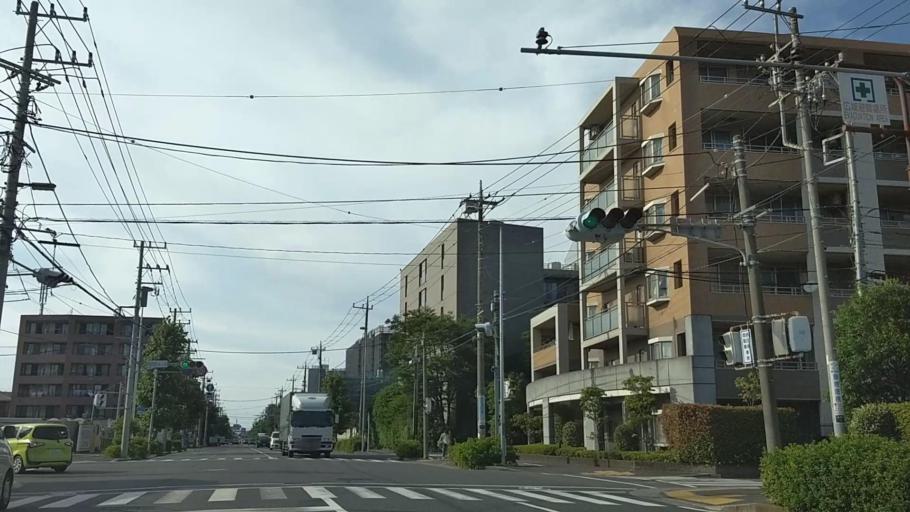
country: JP
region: Kanagawa
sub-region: Kawasaki-shi
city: Kawasaki
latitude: 35.5048
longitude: 139.6936
